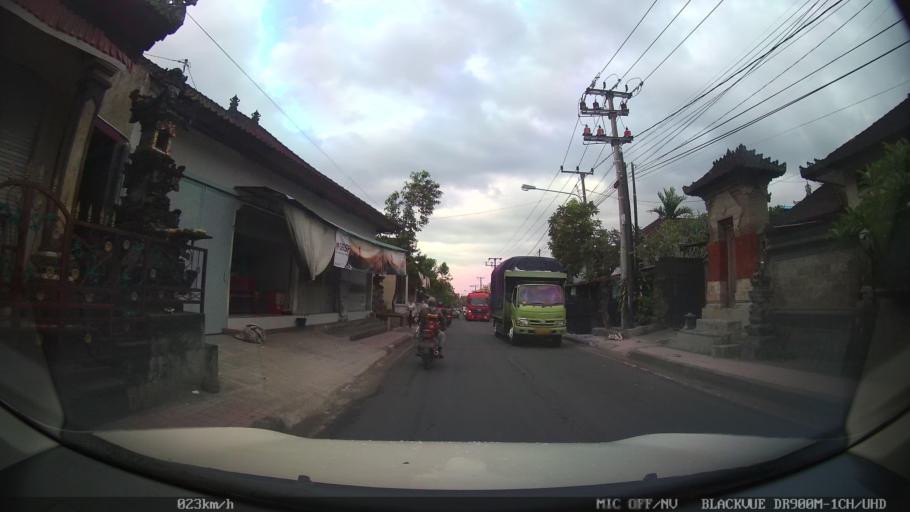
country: ID
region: Bali
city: Banjar Pasekan
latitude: -8.6291
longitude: 115.2845
